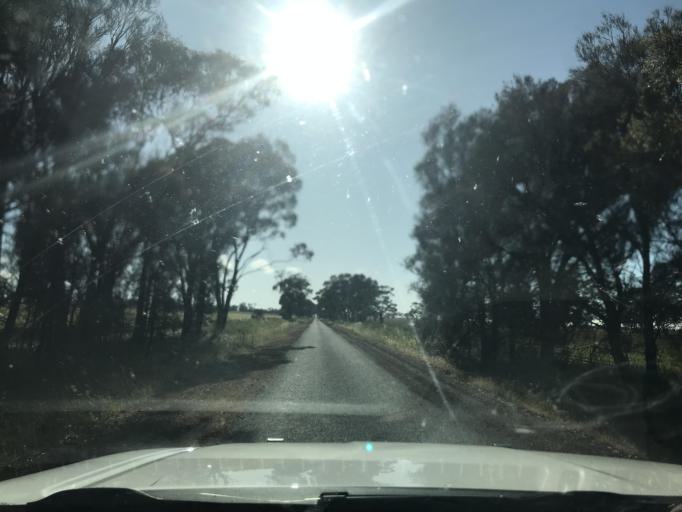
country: AU
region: Victoria
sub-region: Horsham
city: Horsham
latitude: -36.6935
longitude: 141.5586
